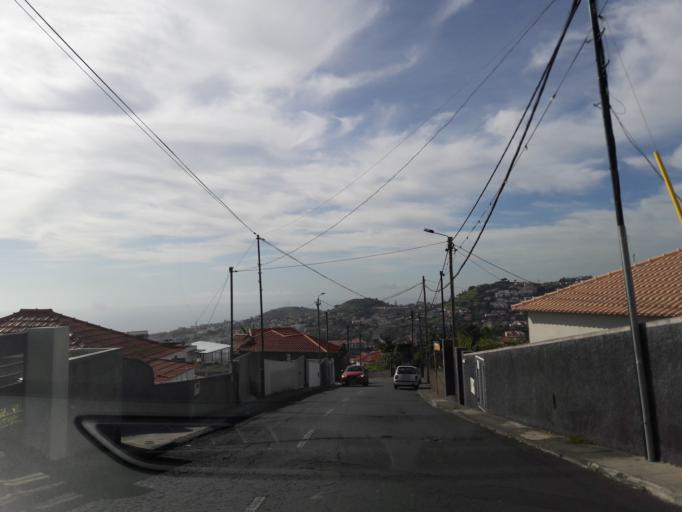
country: PT
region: Madeira
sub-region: Funchal
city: Nossa Senhora do Monte
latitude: 32.6712
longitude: -16.9262
